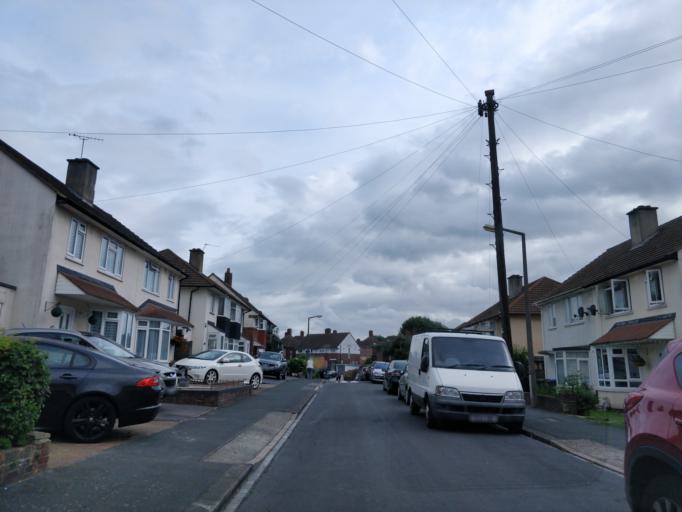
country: GB
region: England
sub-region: Greater London
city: Chislehurst
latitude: 51.4302
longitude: 0.0595
